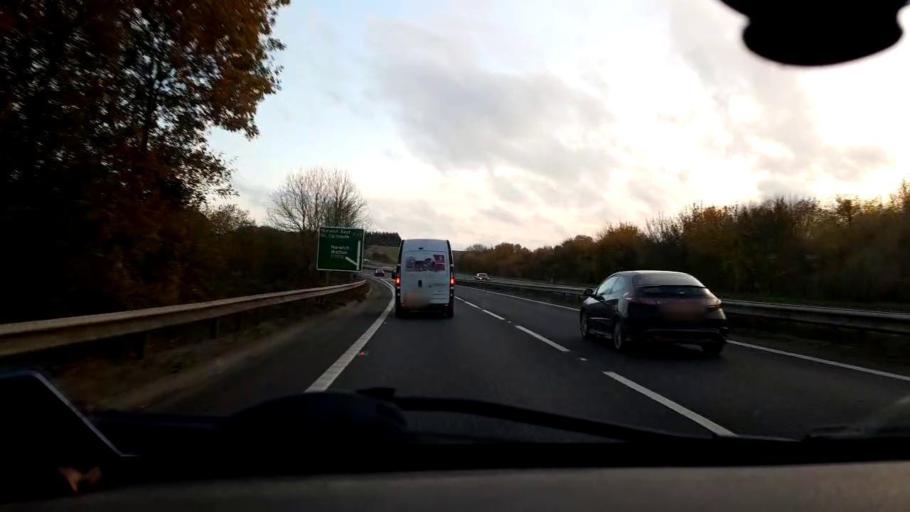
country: GB
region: England
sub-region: Norfolk
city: Bowthorpe
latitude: 52.6307
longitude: 1.1953
